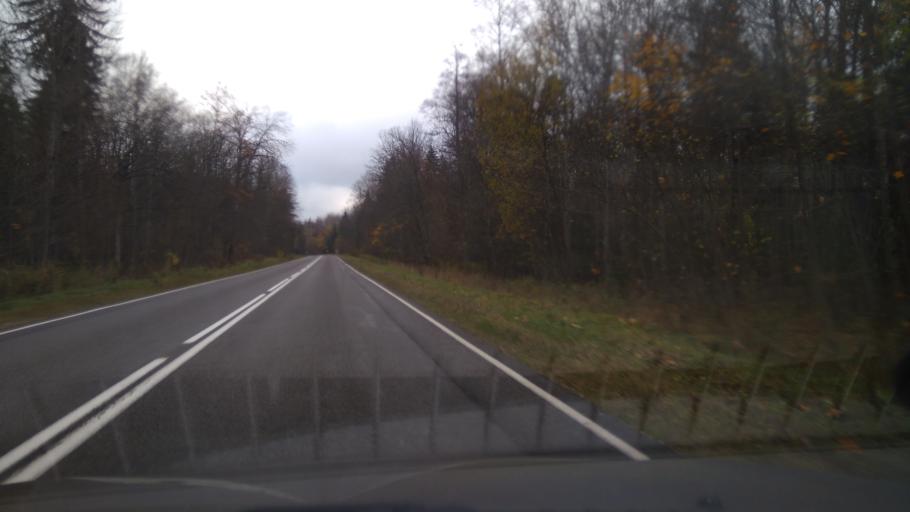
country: BY
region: Minsk
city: Urechcha
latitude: 53.2082
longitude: 27.9120
